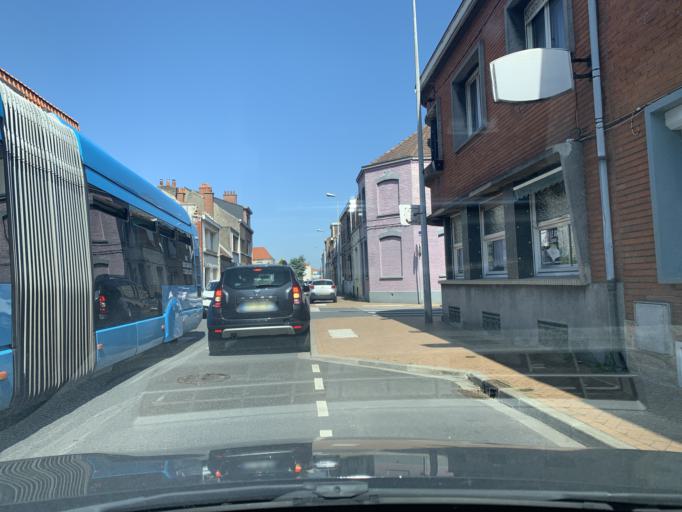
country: FR
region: Nord-Pas-de-Calais
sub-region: Departement du Nord
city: Coudekerque-Branche
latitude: 51.0165
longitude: 2.3839
